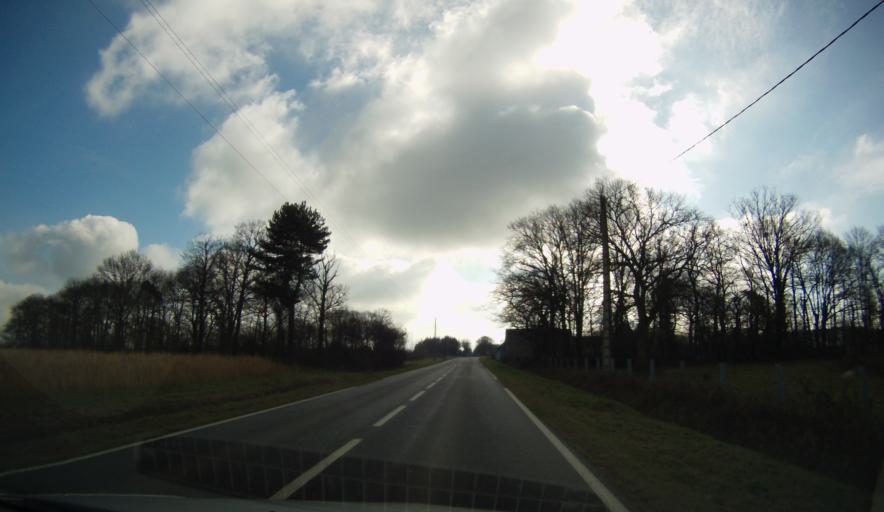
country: FR
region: Brittany
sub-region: Departement d'Ille-et-Vilaine
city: Tresboeuf
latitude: 47.9297
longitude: -1.5516
